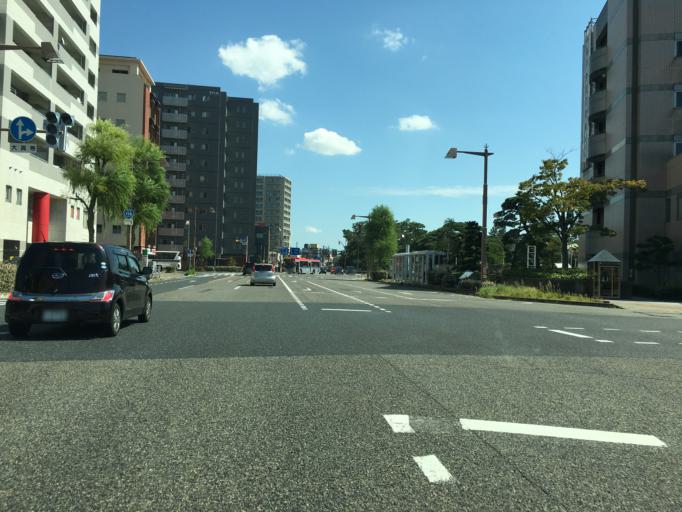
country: JP
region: Niigata
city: Niigata-shi
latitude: 37.9170
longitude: 139.0363
